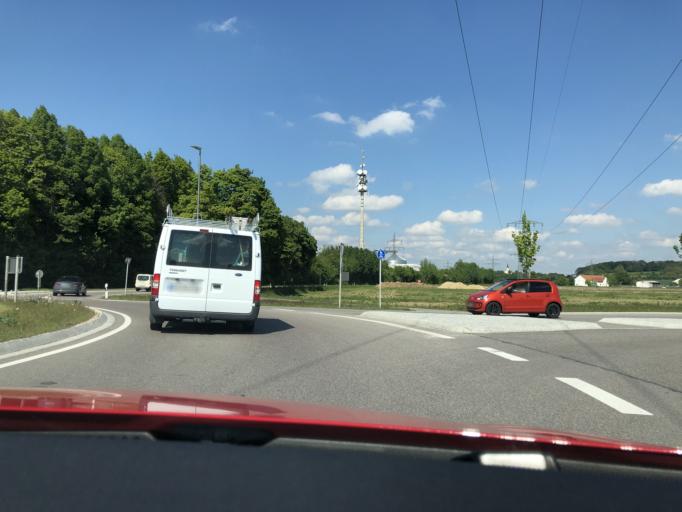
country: DE
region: Bavaria
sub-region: Upper Bavaria
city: Grossmehring
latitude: 48.7827
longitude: 11.5050
